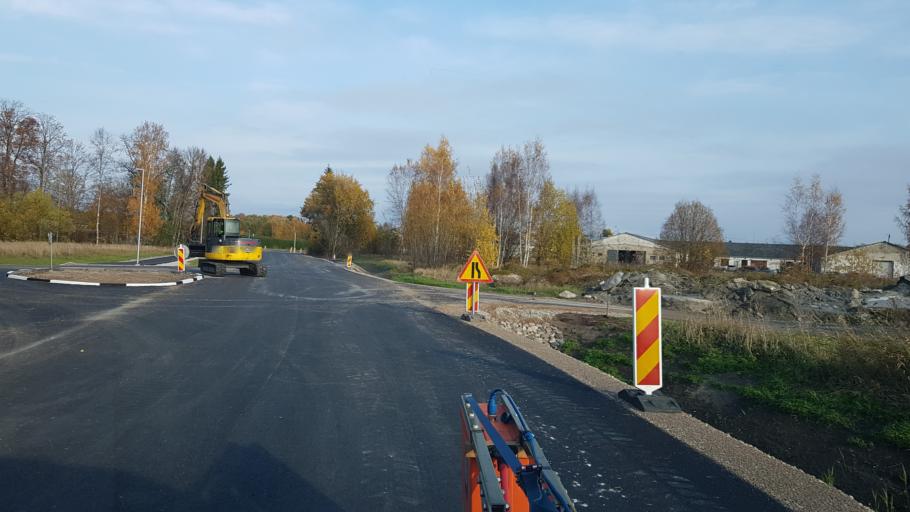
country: EE
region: Paernumaa
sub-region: Paikuse vald
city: Paikuse
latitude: 58.3401
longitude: 24.6208
